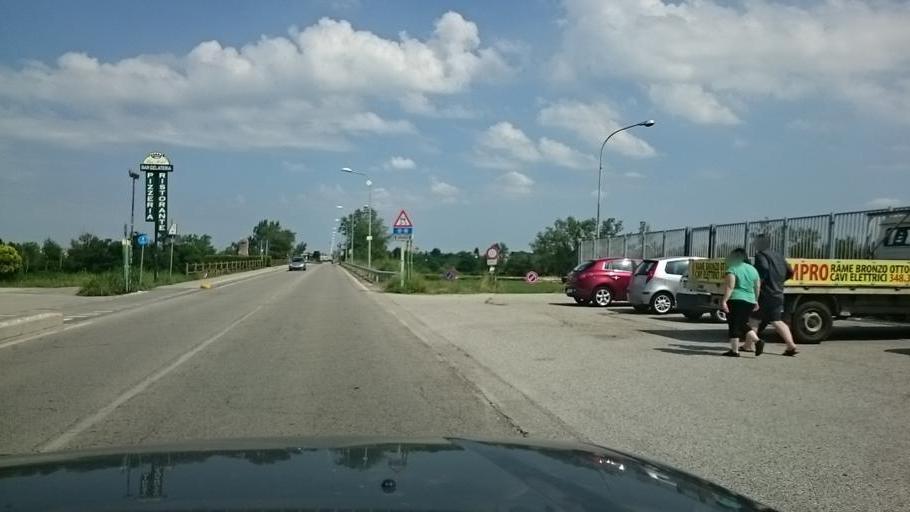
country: IT
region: Veneto
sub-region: Provincia di Vicenza
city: Nove
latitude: 45.7236
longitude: 11.6890
